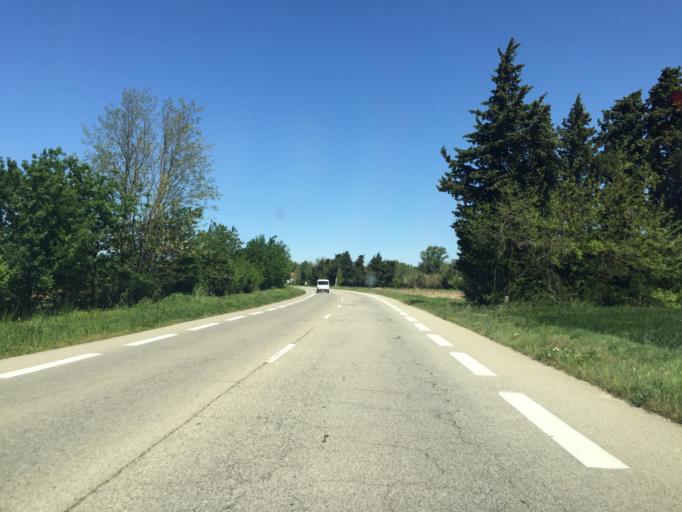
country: FR
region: Provence-Alpes-Cote d'Azur
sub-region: Departement du Vaucluse
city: Jonquieres
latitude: 44.1139
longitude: 4.9236
